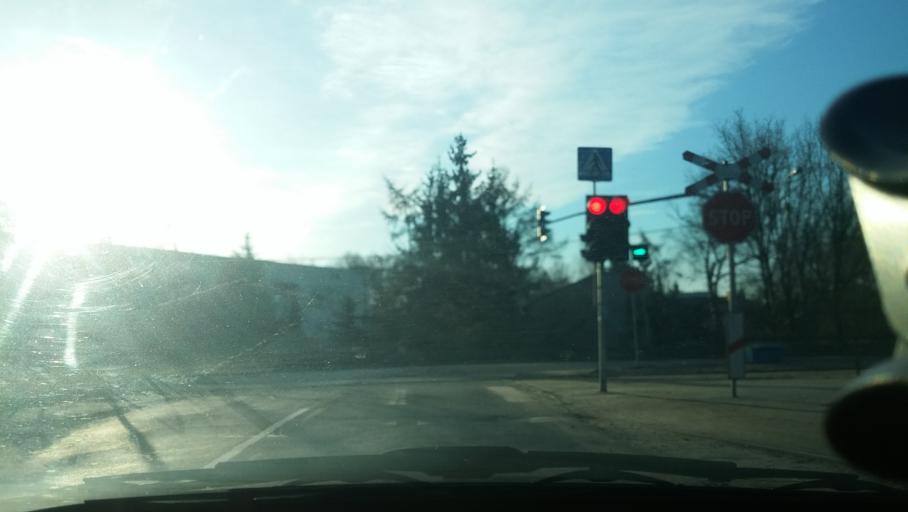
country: PL
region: Masovian Voivodeship
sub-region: Powiat piaseczynski
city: Piaseczno
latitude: 52.0658
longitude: 21.0192
